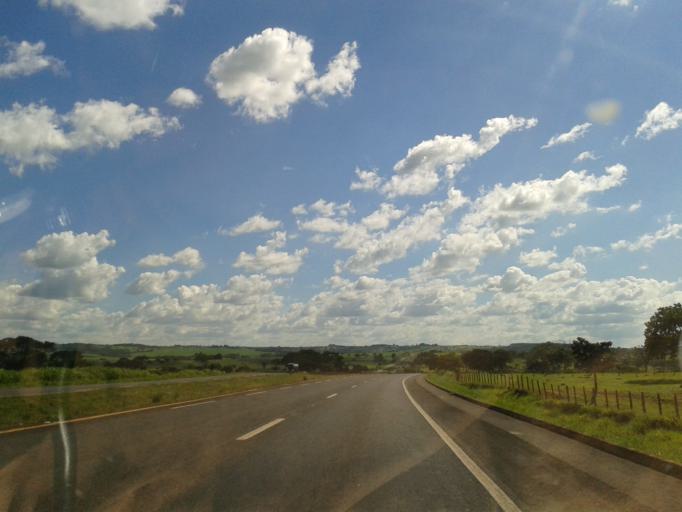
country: BR
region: Goias
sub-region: Morrinhos
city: Morrinhos
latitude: -17.7586
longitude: -49.1634
